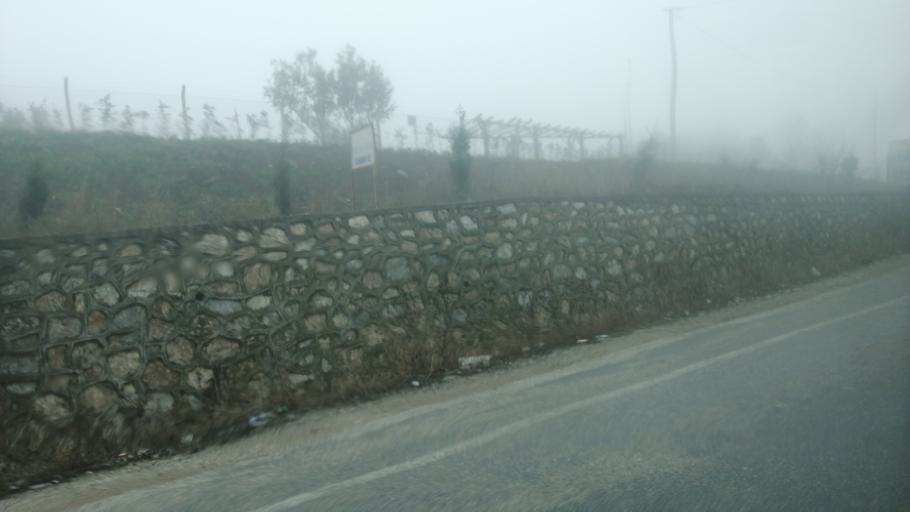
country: TR
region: Yalova
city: Korukoy
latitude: 40.6526
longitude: 29.1774
